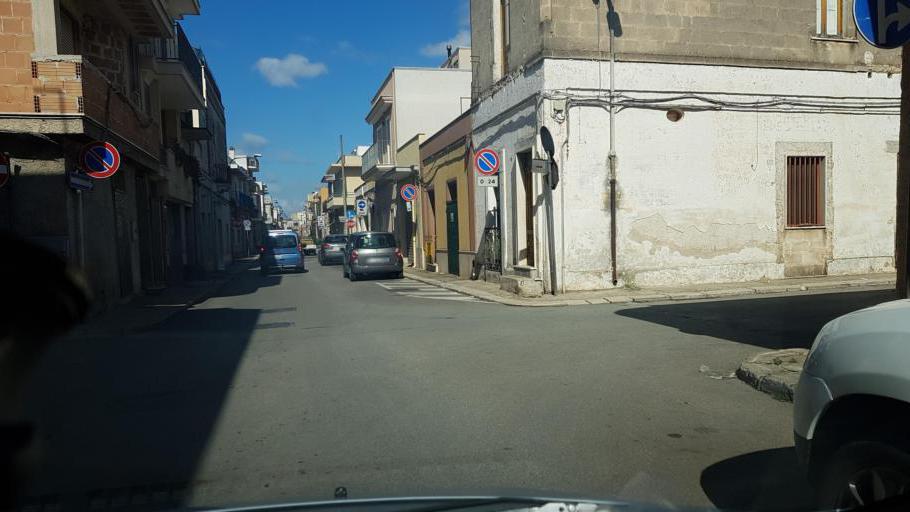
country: IT
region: Apulia
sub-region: Provincia di Brindisi
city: San Vito dei Normanni
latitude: 40.6534
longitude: 17.7090
